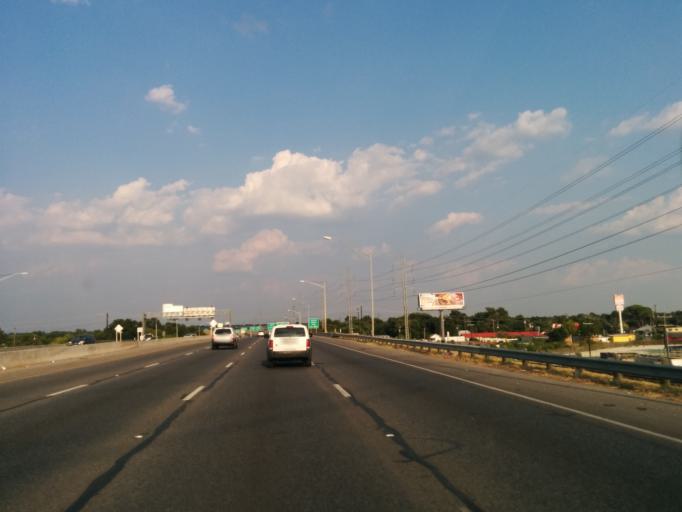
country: US
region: Texas
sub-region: Bexar County
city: San Antonio
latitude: 29.3949
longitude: -98.4890
